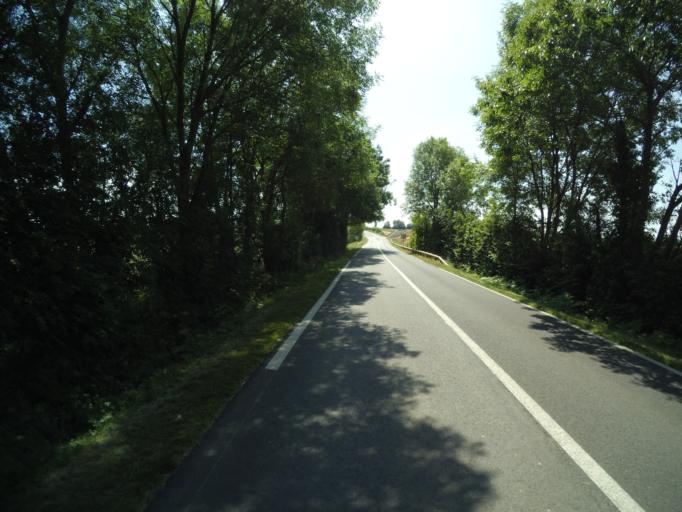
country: FR
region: Pays de la Loire
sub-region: Departement de la Vendee
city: Saint-Michel-Mont-Mercure
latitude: 46.8192
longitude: -0.8729
